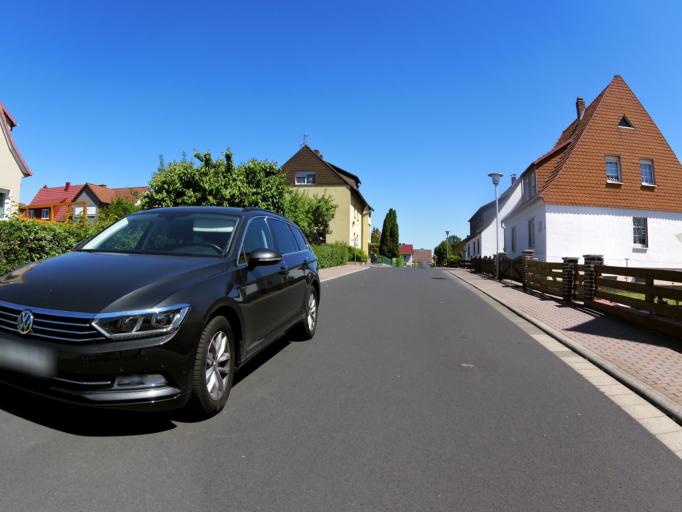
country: DE
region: Thuringia
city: Dankmarshausen
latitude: 50.9465
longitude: 10.0271
